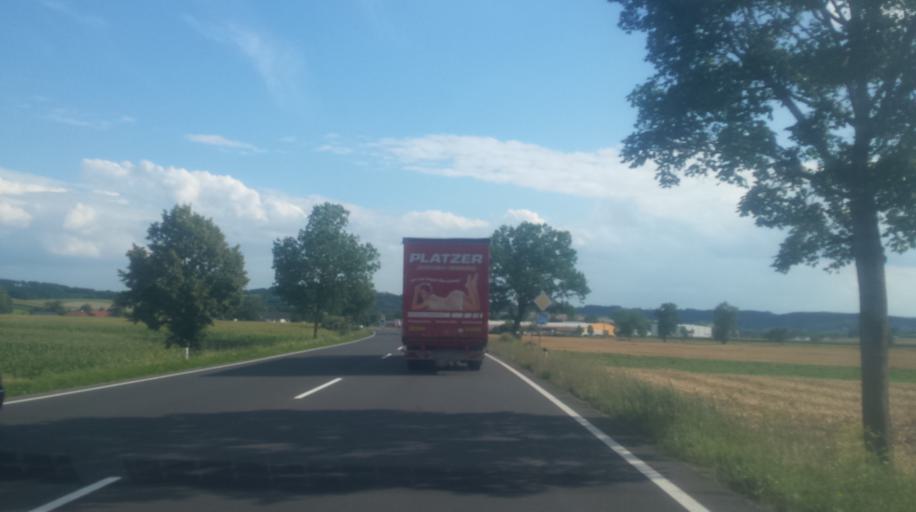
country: AT
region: Upper Austria
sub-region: Politischer Bezirk Grieskirchen
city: Bad Schallerbach
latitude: 48.2092
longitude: 13.9248
